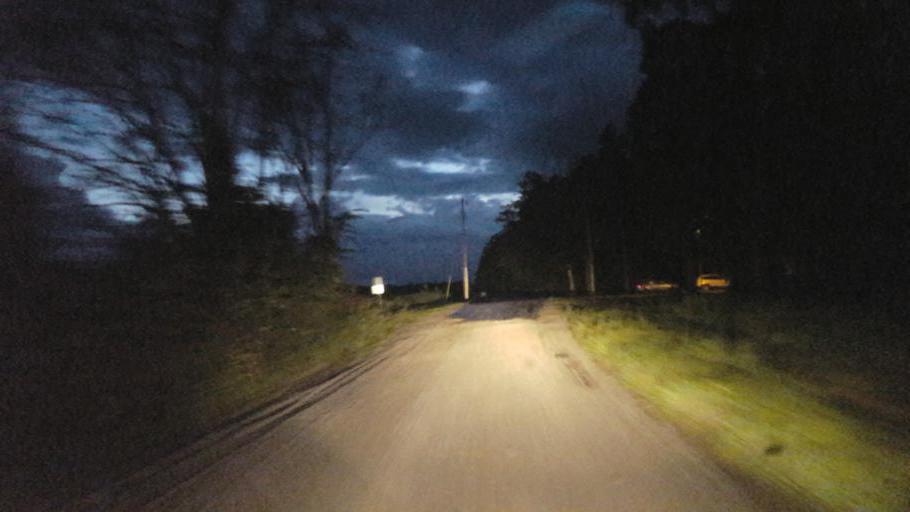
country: US
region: Ohio
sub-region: Richland County
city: Lexington
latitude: 40.5941
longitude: -82.6901
